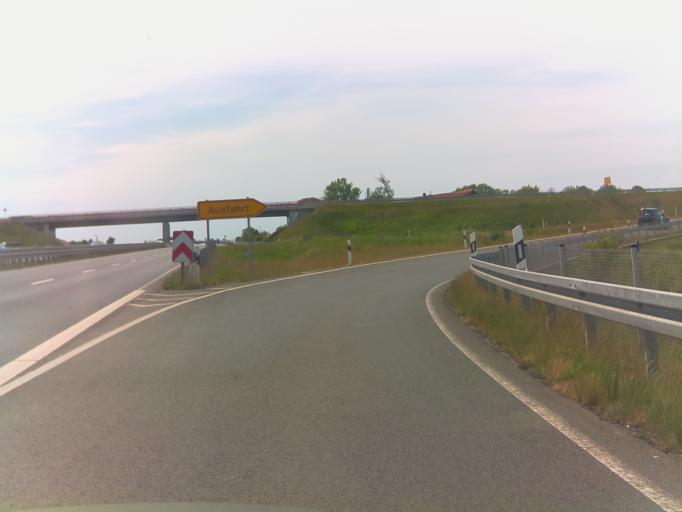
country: DE
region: Saxony-Anhalt
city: Wolmirsleben
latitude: 52.0025
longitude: 11.4962
